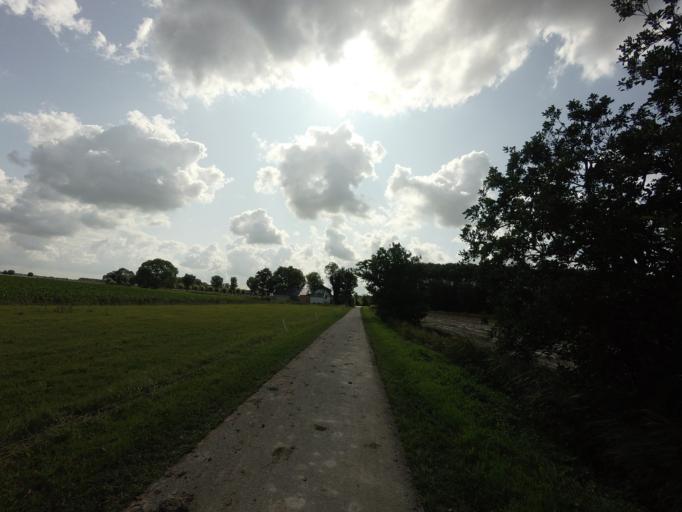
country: NL
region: Friesland
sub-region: Gemeente Het Bildt
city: Minnertsga
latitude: 53.2590
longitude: 5.5969
